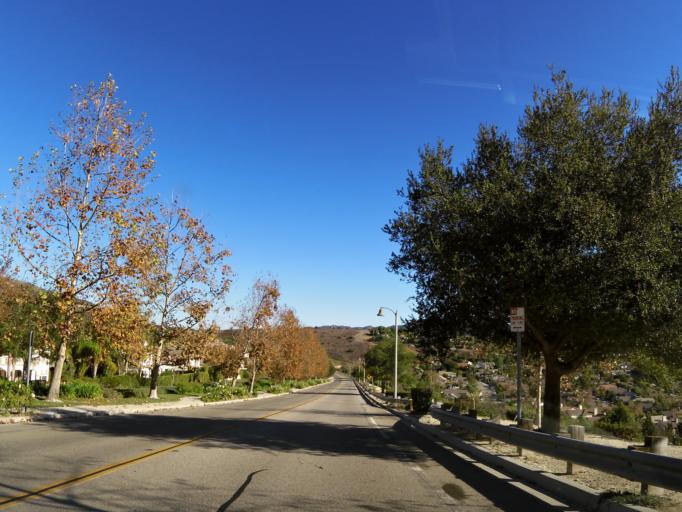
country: US
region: California
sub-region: Ventura County
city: Thousand Oaks
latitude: 34.2235
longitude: -118.8362
